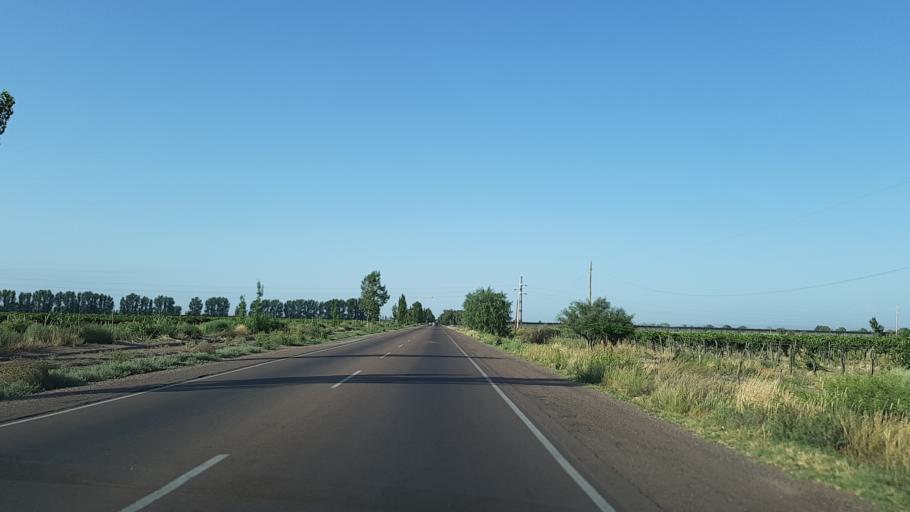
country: AR
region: Mendoza
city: San Martin
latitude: -33.0002
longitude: -68.4793
